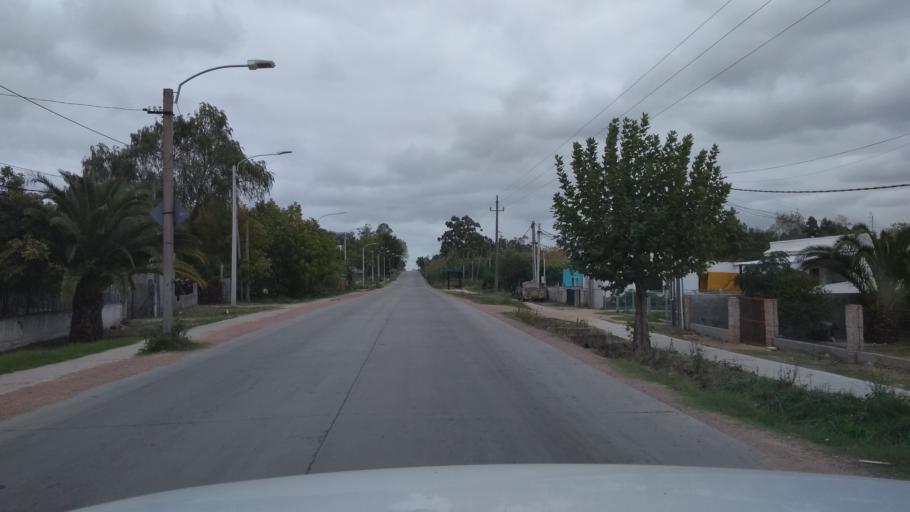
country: UY
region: Canelones
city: Toledo
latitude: -34.7842
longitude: -56.1394
